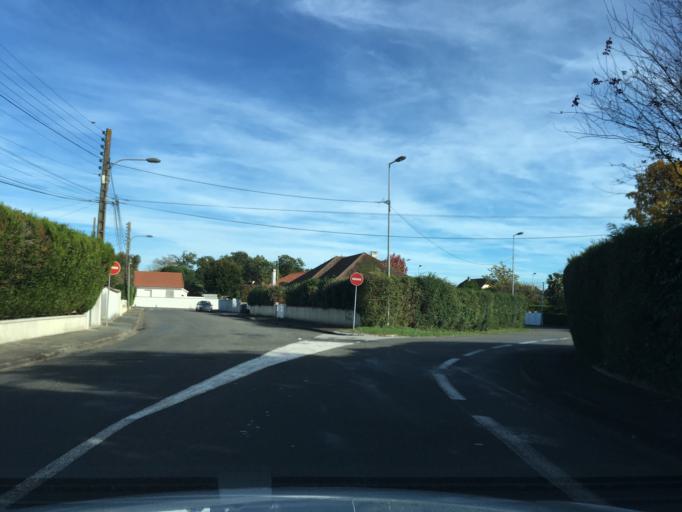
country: FR
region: Aquitaine
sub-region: Departement des Pyrenees-Atlantiques
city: Pau
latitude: 43.3283
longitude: -0.3624
